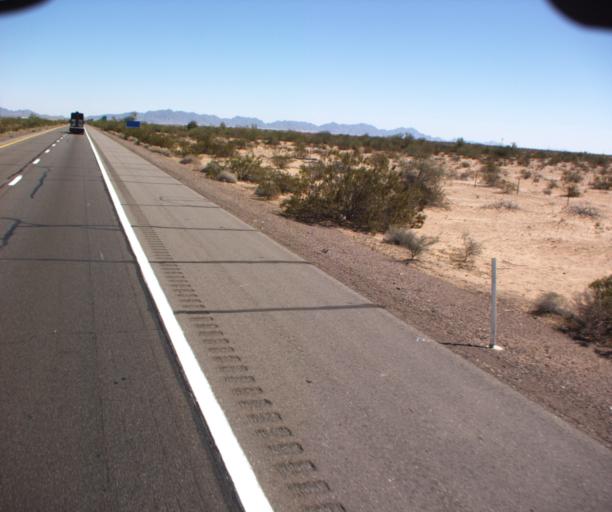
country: US
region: Arizona
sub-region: Yuma County
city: Wellton
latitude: 32.6894
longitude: -113.9793
